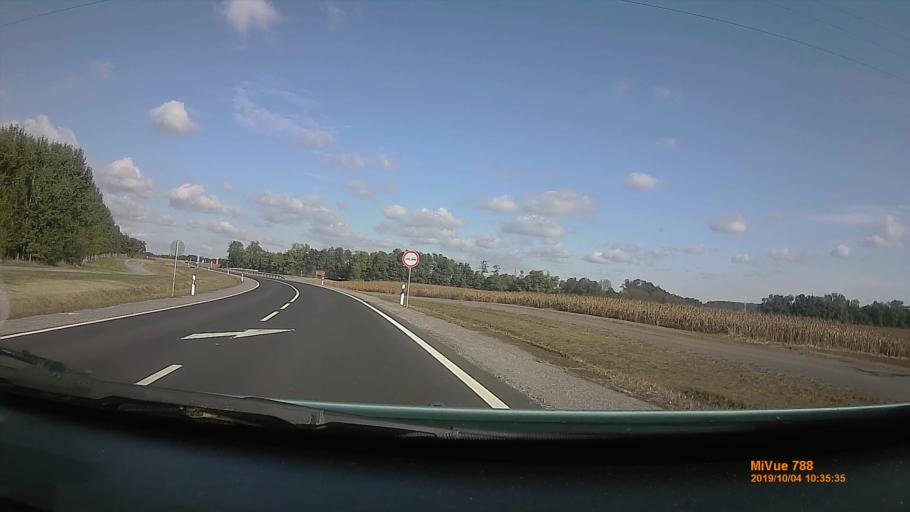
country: HU
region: Szabolcs-Szatmar-Bereg
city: Nyirtelek
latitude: 47.9648
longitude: 21.6579
